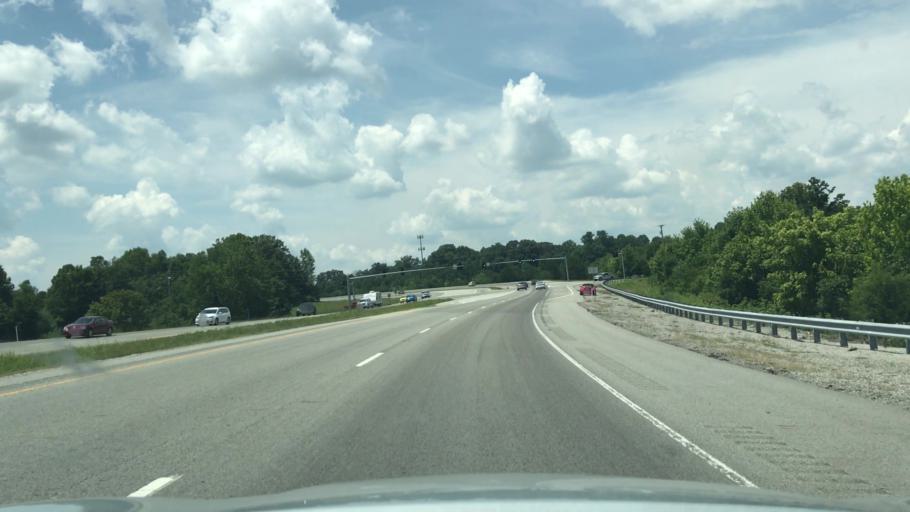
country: US
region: Tennessee
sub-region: Putnam County
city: Algood
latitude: 36.2044
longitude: -85.4557
